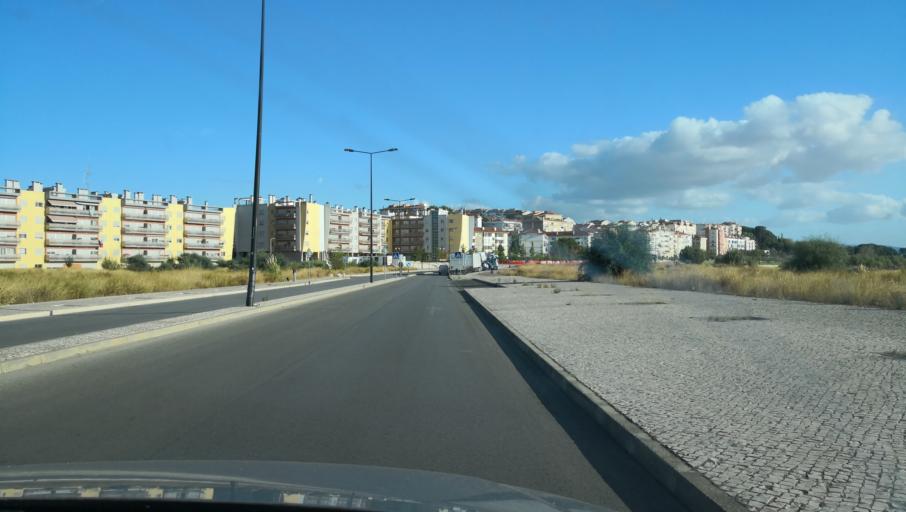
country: PT
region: Setubal
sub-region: Barreiro
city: Barreiro
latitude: 38.6502
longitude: -9.0667
